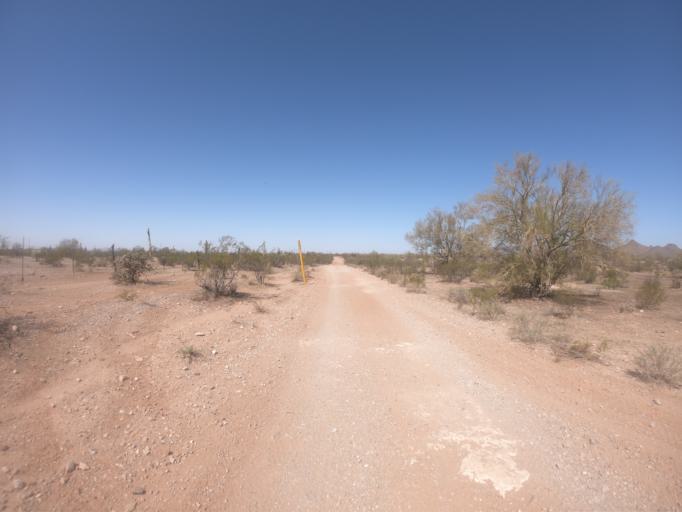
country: US
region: Arizona
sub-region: Pinal County
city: Gold Camp
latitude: 33.2432
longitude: -111.3204
